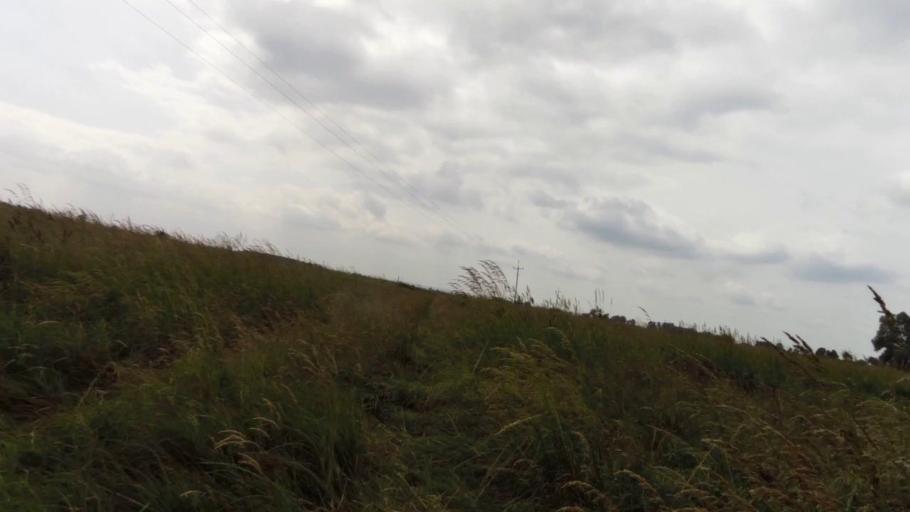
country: PL
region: West Pomeranian Voivodeship
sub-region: Powiat goleniowski
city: Goleniow
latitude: 53.4975
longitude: 14.7057
